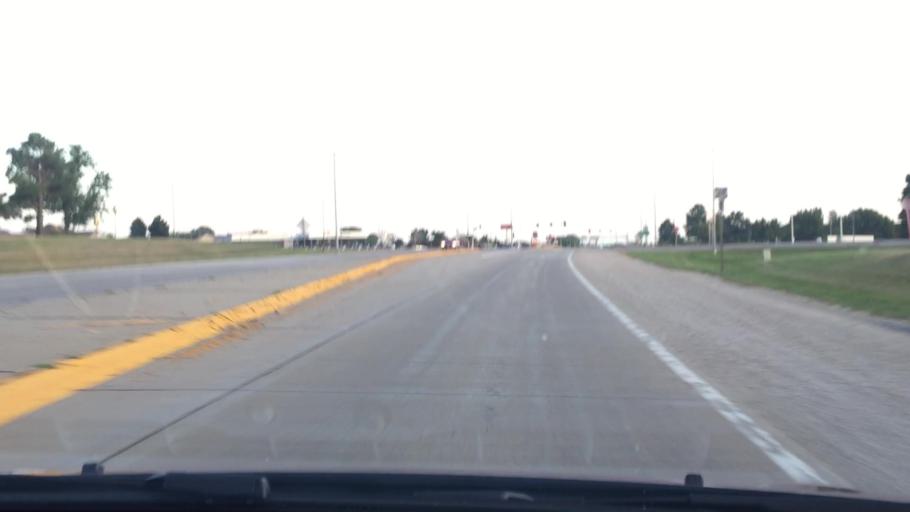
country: US
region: Iowa
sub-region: Muscatine County
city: Muscatine
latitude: 41.4563
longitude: -91.0303
